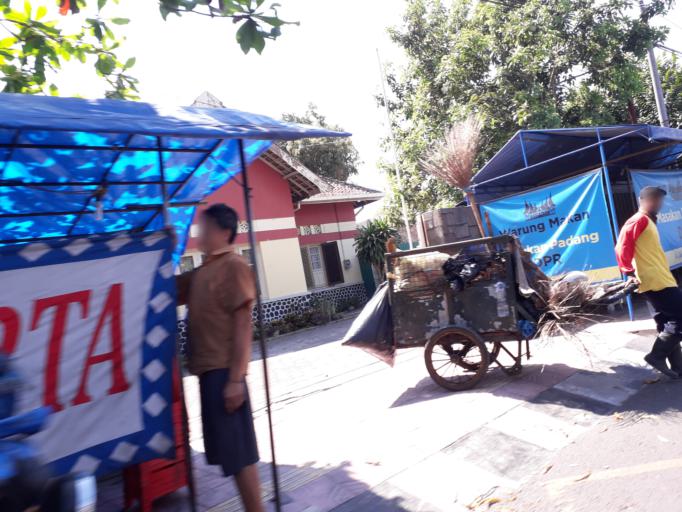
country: ID
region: Daerah Istimewa Yogyakarta
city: Yogyakarta
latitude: -7.7773
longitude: 110.3759
